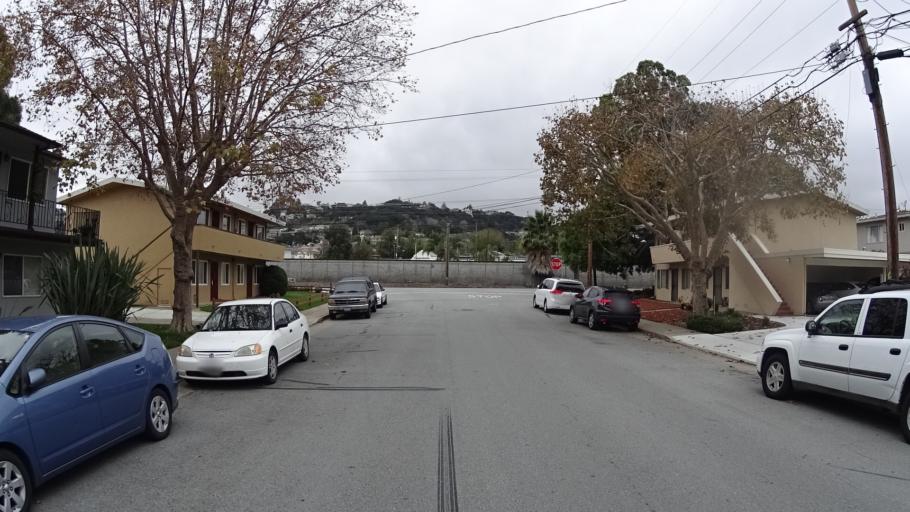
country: US
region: California
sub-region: San Mateo County
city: Belmont
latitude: 37.5324
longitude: -122.2901
